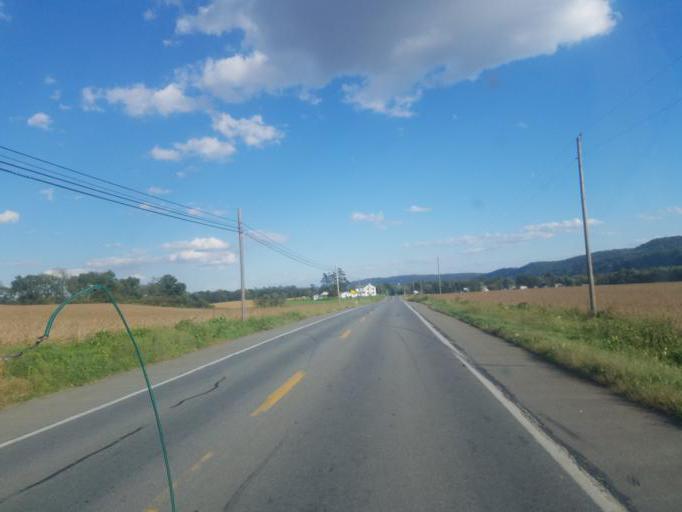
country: US
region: Pennsylvania
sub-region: Lancaster County
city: Maytown
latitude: 40.0684
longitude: -76.6216
